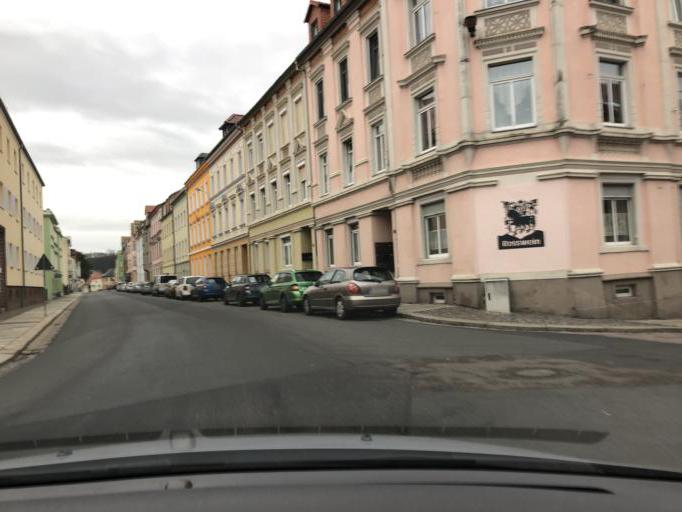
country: DE
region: Saxony
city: Rosswein
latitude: 51.0651
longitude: 13.1777
